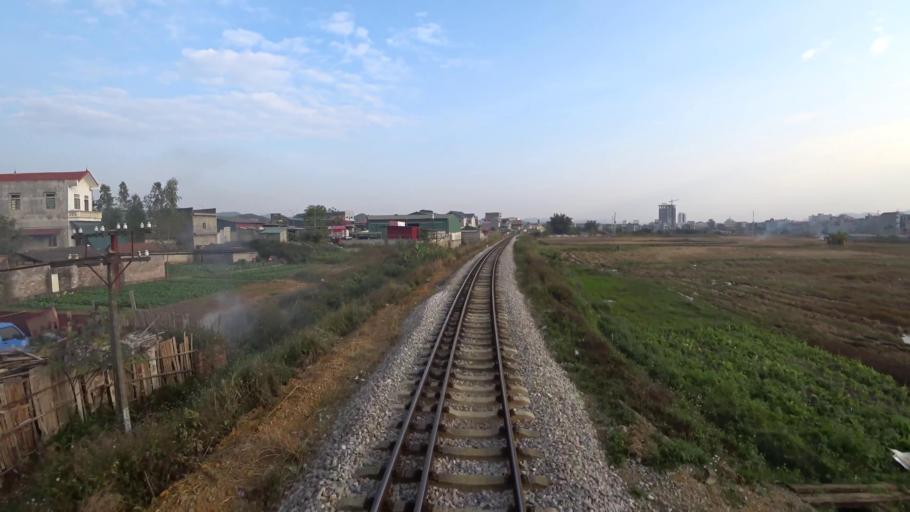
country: VN
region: Lang Son
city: Thi Tran Cao Loc
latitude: 21.8741
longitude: 106.7522
